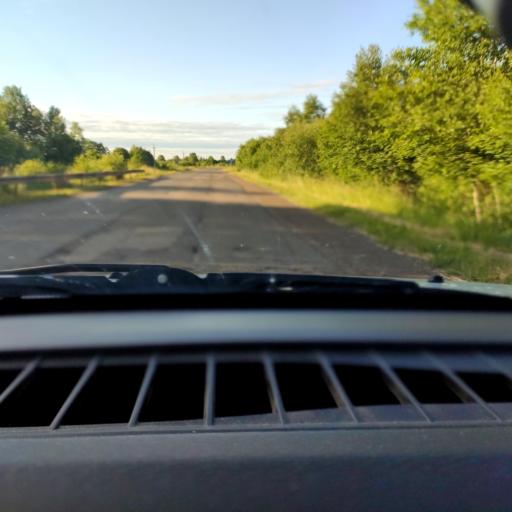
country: RU
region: Perm
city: Uinskoye
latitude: 57.0897
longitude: 56.5564
